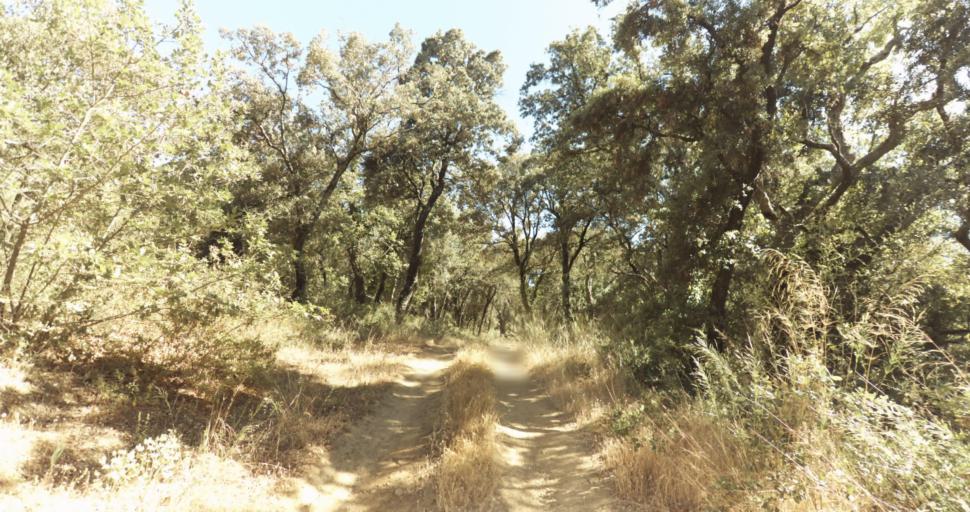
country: FR
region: Provence-Alpes-Cote d'Azur
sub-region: Departement du Var
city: Gassin
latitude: 43.2451
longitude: 6.5845
